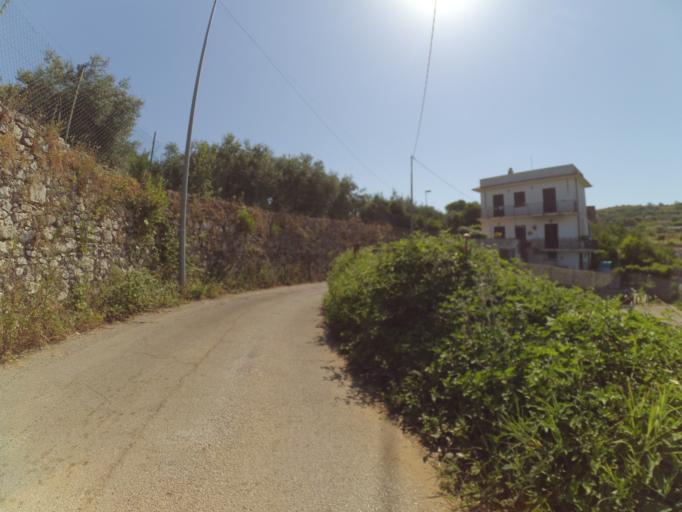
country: IT
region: Latium
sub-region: Provincia di Latina
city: Gaeta
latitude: 41.2185
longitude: 13.5526
